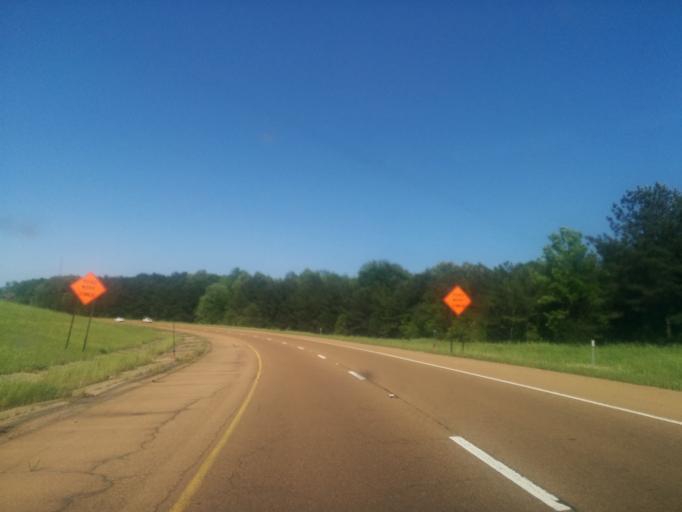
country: US
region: Mississippi
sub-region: Madison County
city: Ridgeland
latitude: 32.4131
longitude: -90.1476
